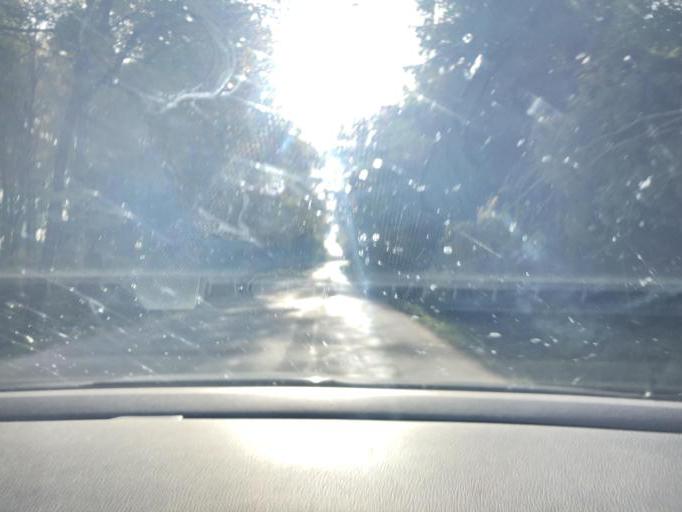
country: CZ
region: Central Bohemia
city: Postupice
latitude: 49.7717
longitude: 14.7925
